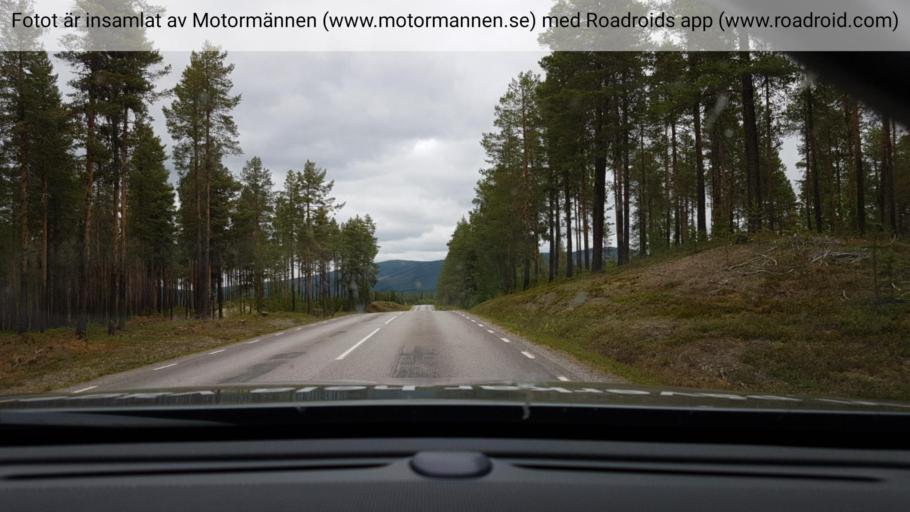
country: SE
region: Vaesterbotten
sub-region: Sorsele Kommun
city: Sorsele
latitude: 65.6084
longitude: 17.4879
